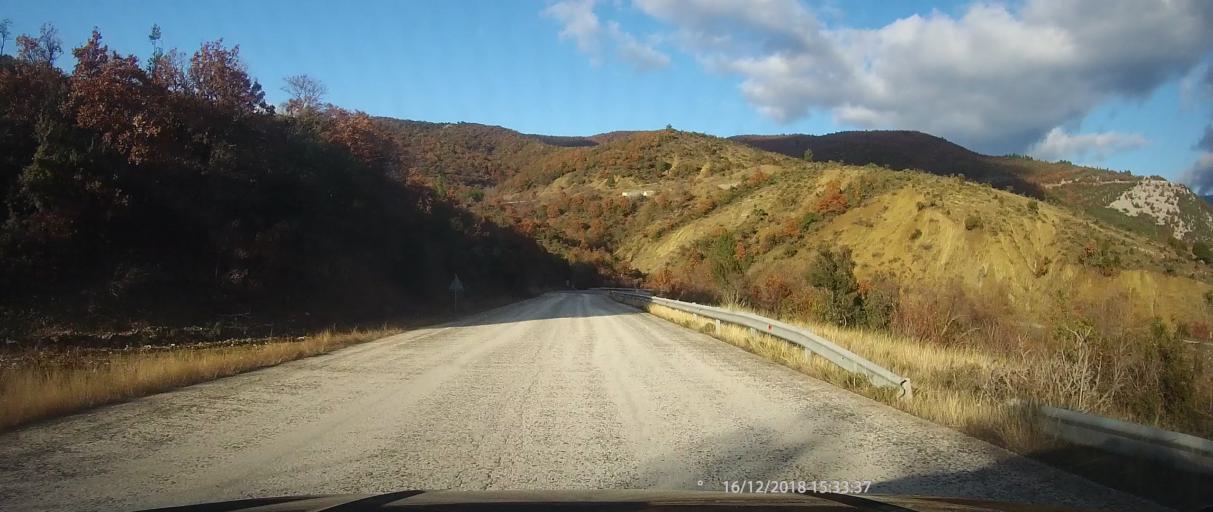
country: GR
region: Epirus
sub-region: Nomos Ioanninon
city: Konitsa
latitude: 40.0631
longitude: 20.7368
